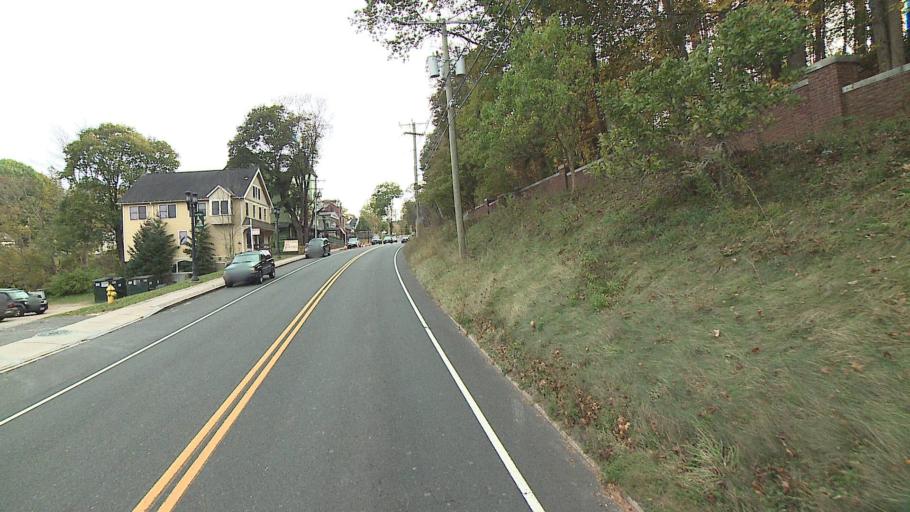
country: US
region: Connecticut
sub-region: Litchfield County
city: Winchester Center
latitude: 41.9914
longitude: -73.2005
